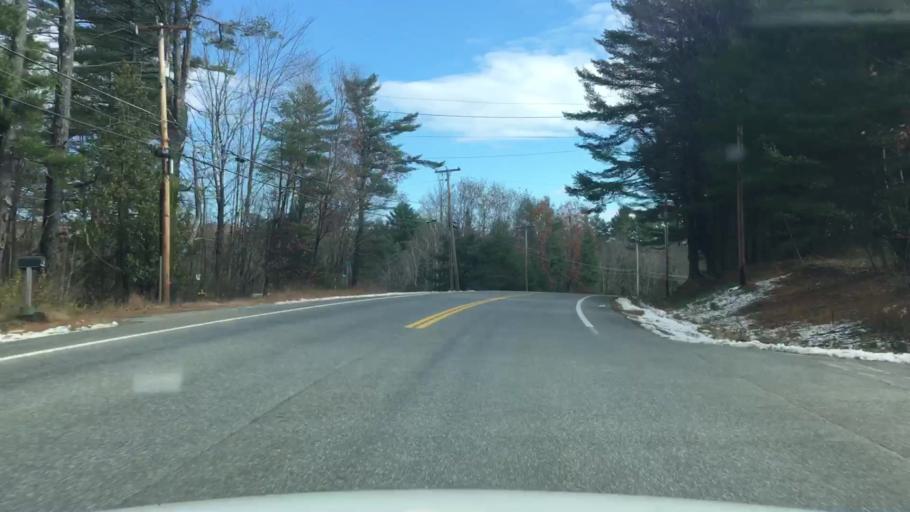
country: US
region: Maine
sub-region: Kennebec County
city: Wayne
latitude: 44.3494
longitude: -70.0513
